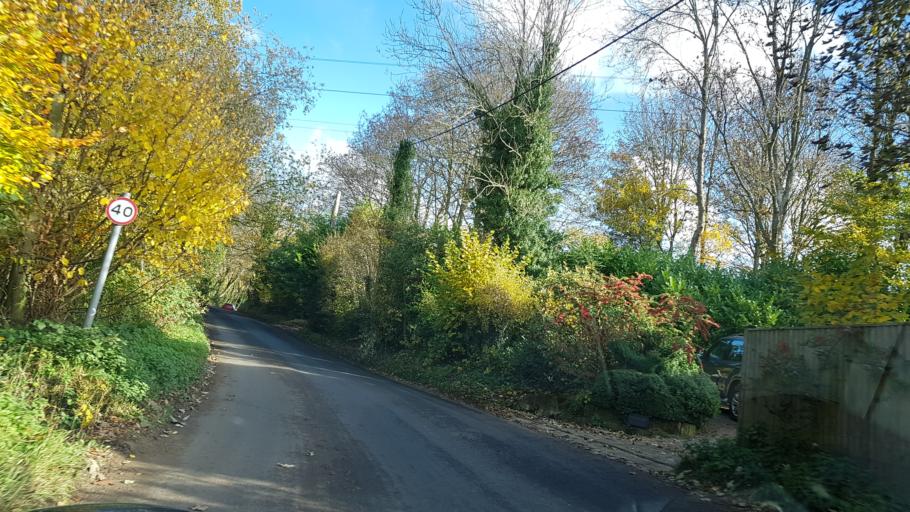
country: GB
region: England
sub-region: Surrey
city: Hindhead
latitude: 51.1440
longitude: -0.7334
